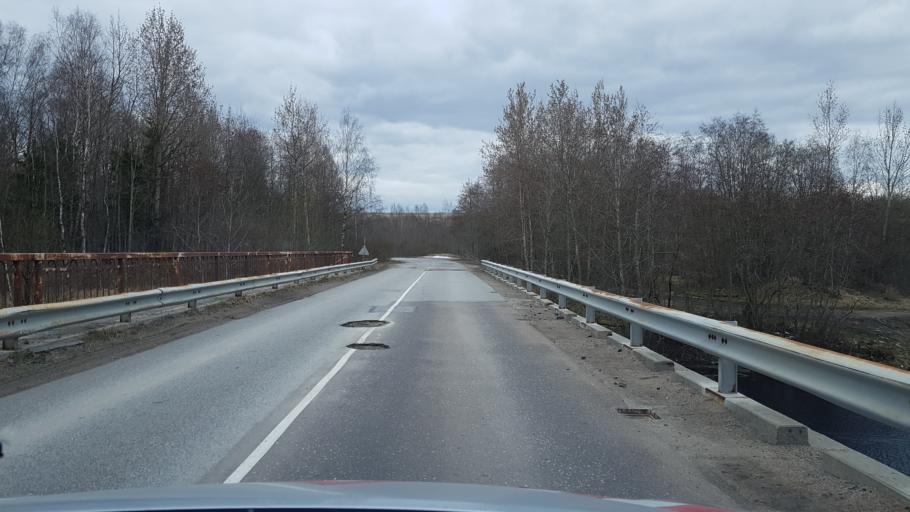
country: EE
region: Ida-Virumaa
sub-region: Narva linn
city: Narva
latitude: 59.3519
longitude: 28.0971
